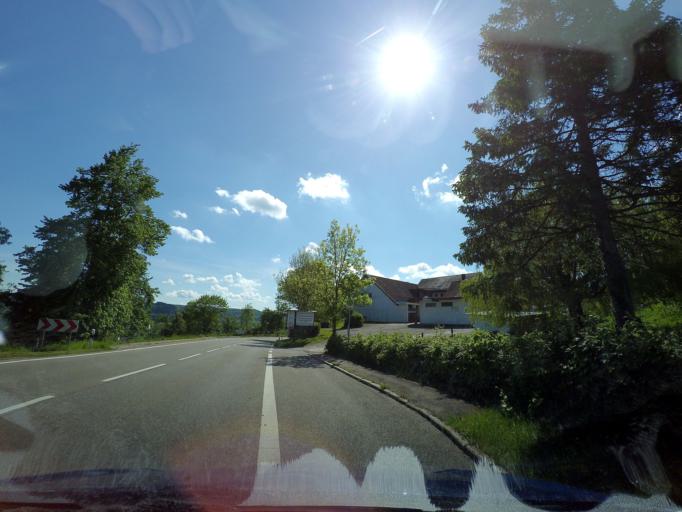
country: DE
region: Baden-Wuerttemberg
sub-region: Regierungsbezirk Stuttgart
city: Gaildorf
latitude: 48.9754
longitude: 9.7674
